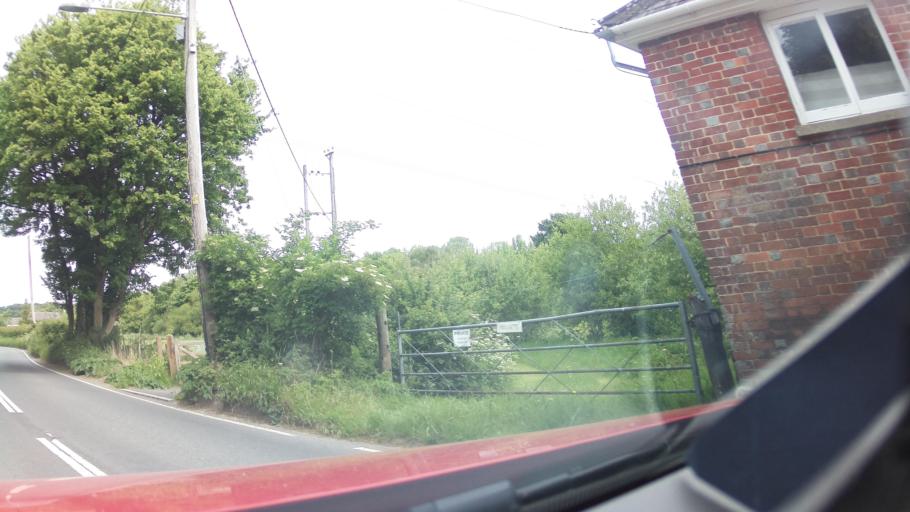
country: GB
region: England
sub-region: Dorset
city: Dorchester
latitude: 50.7382
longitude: -2.4578
